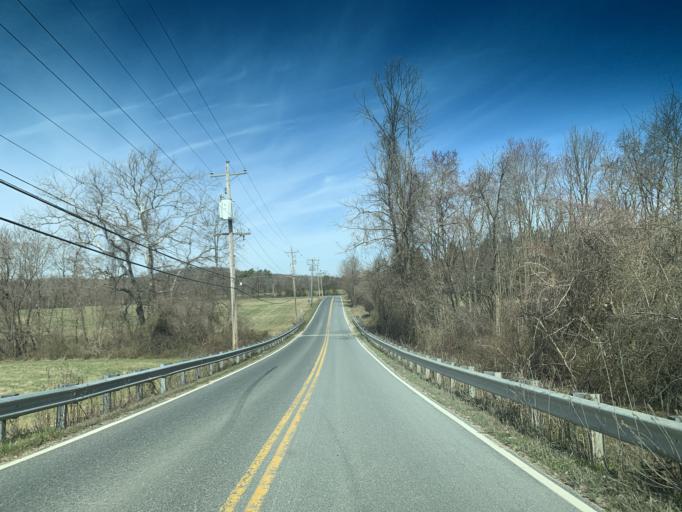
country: US
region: Maryland
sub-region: Cecil County
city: Perryville
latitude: 39.5779
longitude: -76.0261
